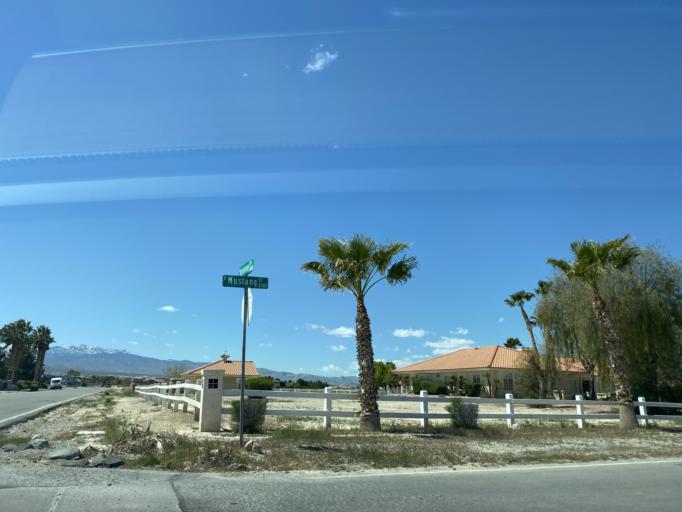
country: US
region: Nevada
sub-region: Clark County
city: North Las Vegas
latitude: 36.3109
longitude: -115.2309
